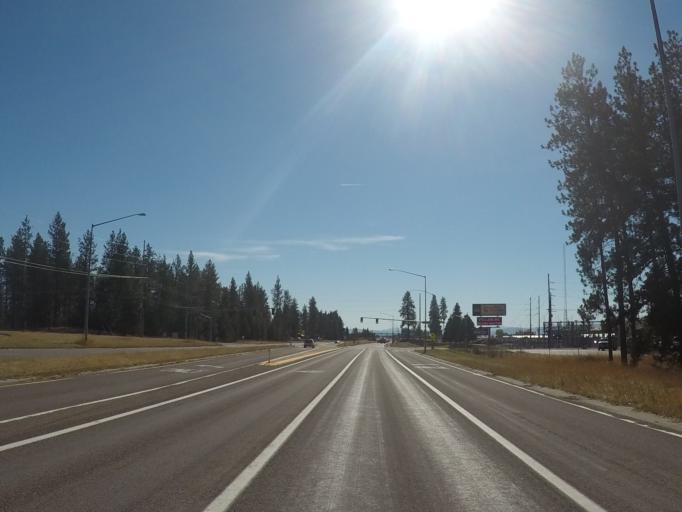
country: US
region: Montana
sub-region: Lake County
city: Pablo
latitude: 47.6034
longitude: -114.1130
